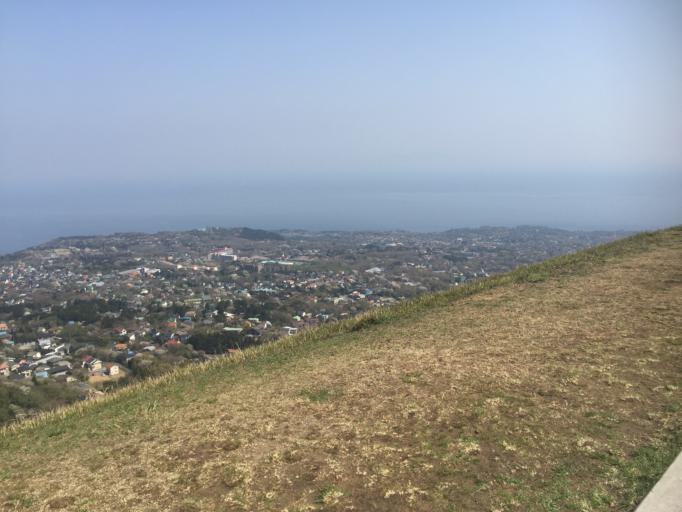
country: JP
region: Shizuoka
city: Ito
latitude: 34.9048
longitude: 139.0971
